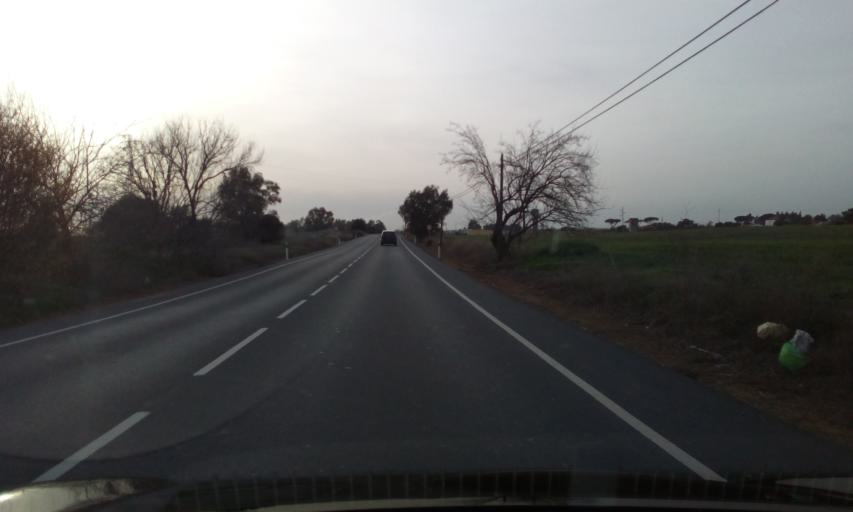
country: ES
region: Andalusia
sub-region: Provincia de Huelva
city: San Juan del Puerto
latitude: 37.3218
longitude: -6.8032
